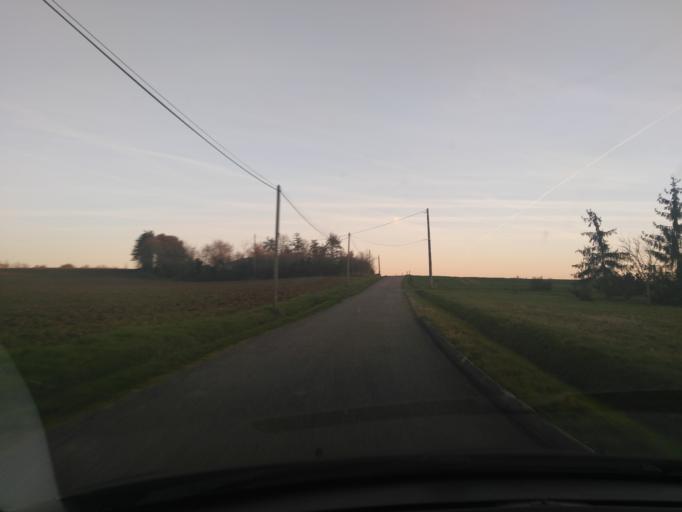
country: FR
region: Aquitaine
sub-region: Departement du Lot-et-Garonne
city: Saint-Hilaire
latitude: 44.4773
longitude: 0.7114
